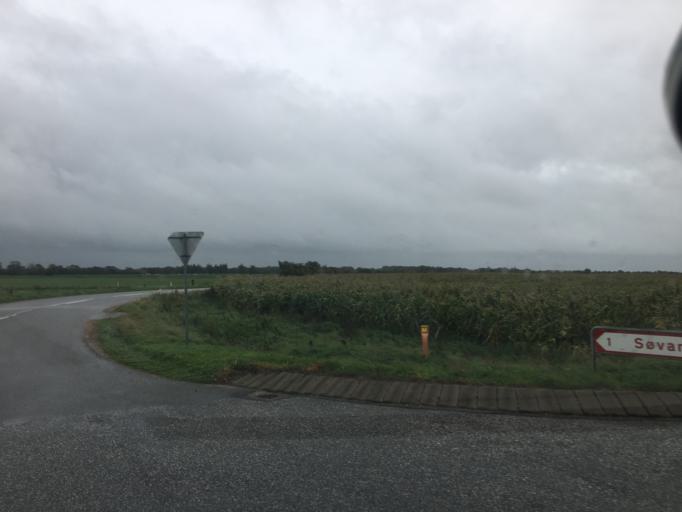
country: DK
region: South Denmark
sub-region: Tonder Kommune
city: Logumkloster
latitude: 54.9883
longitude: 9.0343
